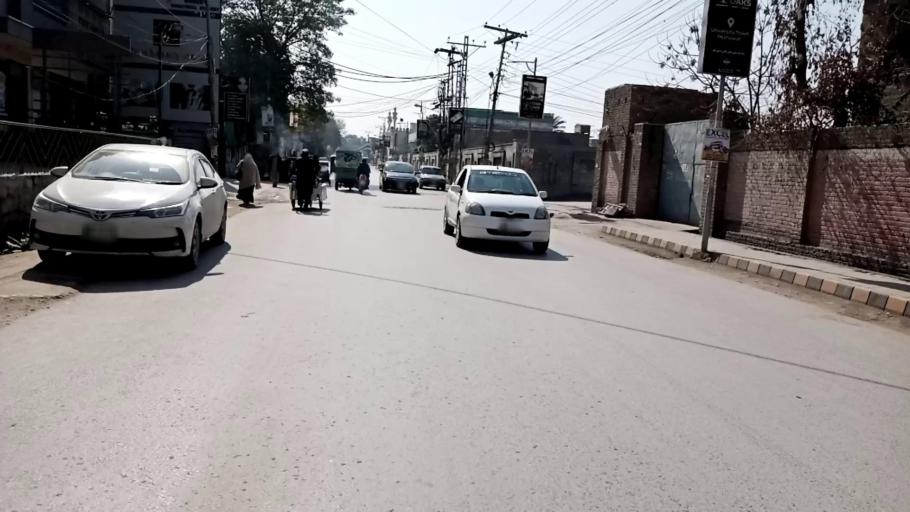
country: PK
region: Khyber Pakhtunkhwa
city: Peshawar
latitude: 34.0006
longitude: 71.5003
